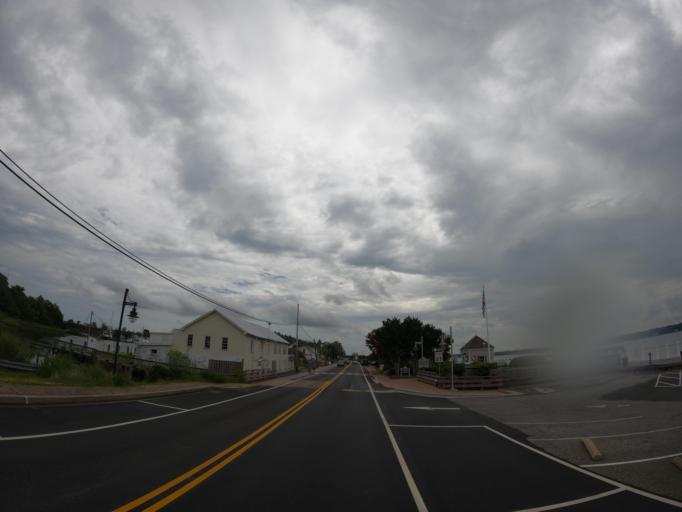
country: US
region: Maryland
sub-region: Calvert County
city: Solomons
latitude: 38.3245
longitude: -76.4615
